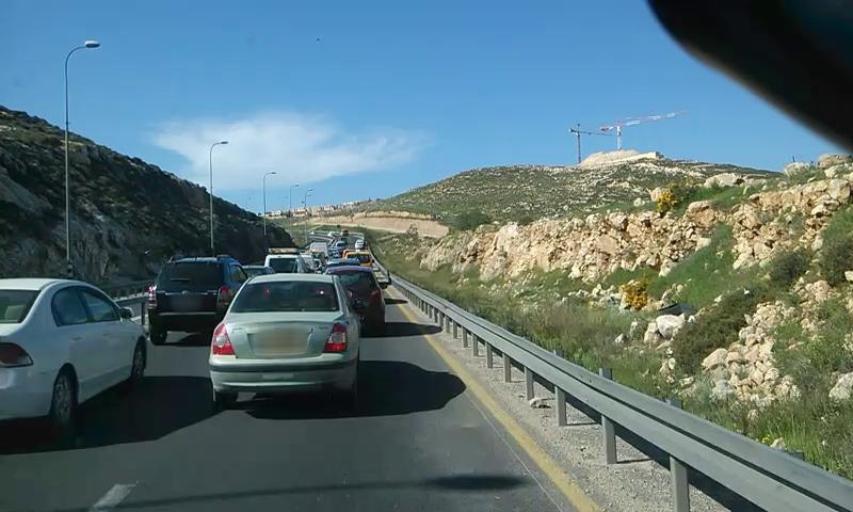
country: PS
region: West Bank
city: Hizma
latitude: 31.8350
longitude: 35.2538
